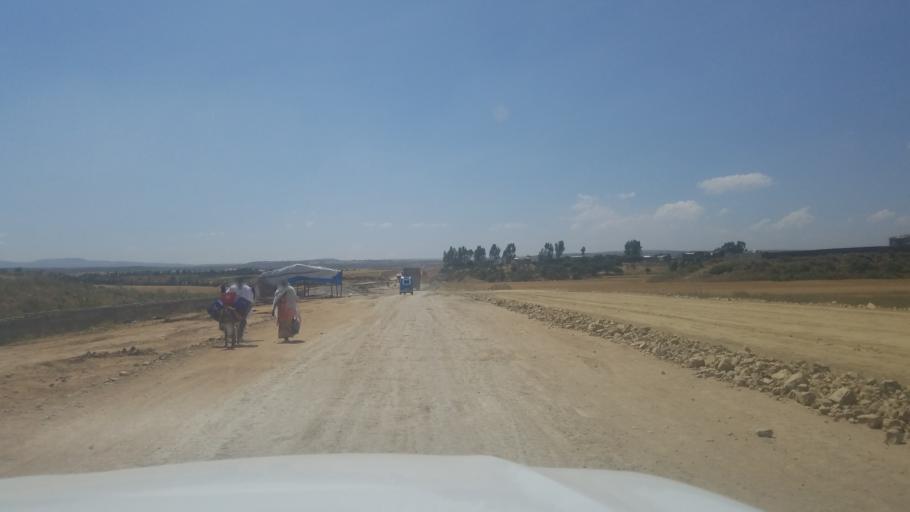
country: ET
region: Tigray
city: Mekele
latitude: 13.7643
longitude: 39.5902
